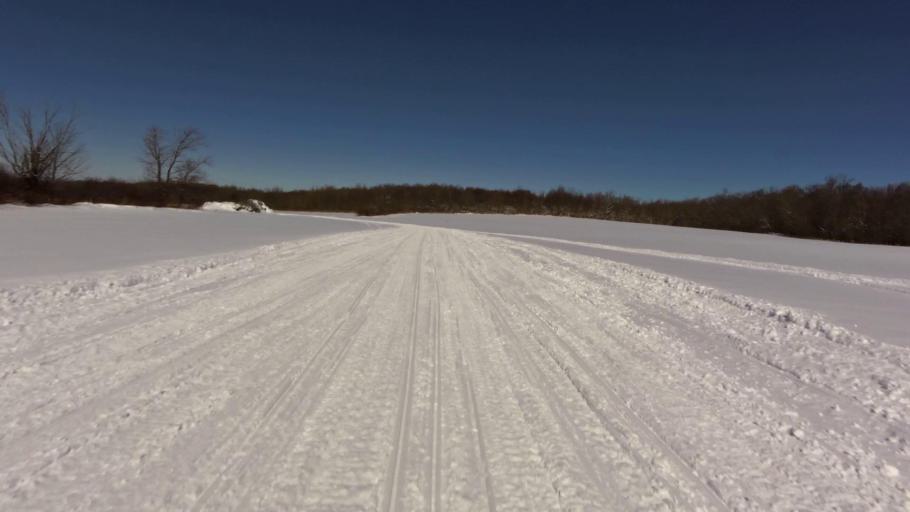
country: US
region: New York
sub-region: Chautauqua County
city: Mayville
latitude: 42.2648
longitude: -79.4507
